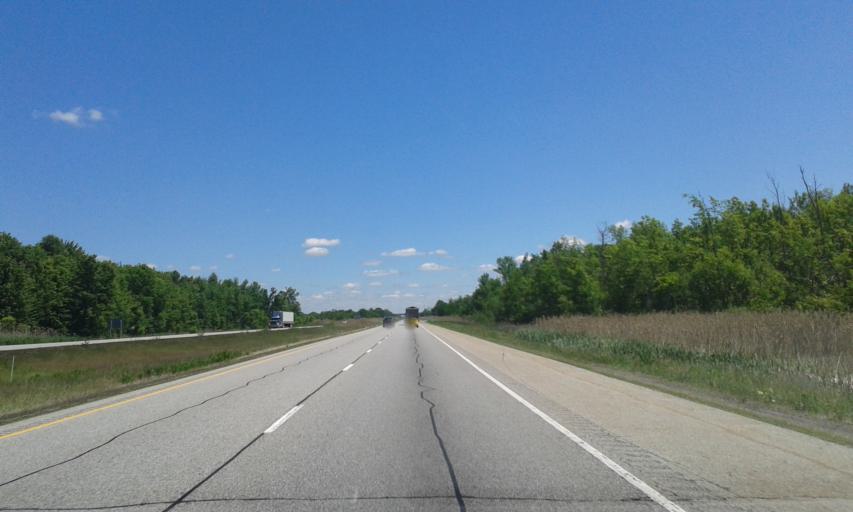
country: US
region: New York
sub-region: St. Lawrence County
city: Norfolk
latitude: 44.9114
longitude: -75.2107
